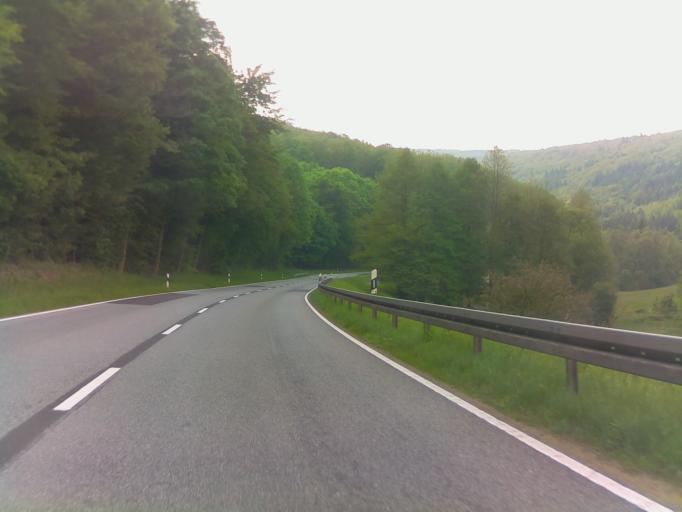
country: DE
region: Bavaria
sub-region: Regierungsbezirk Unterfranken
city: Rechtenbach
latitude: 49.9788
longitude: 9.5176
